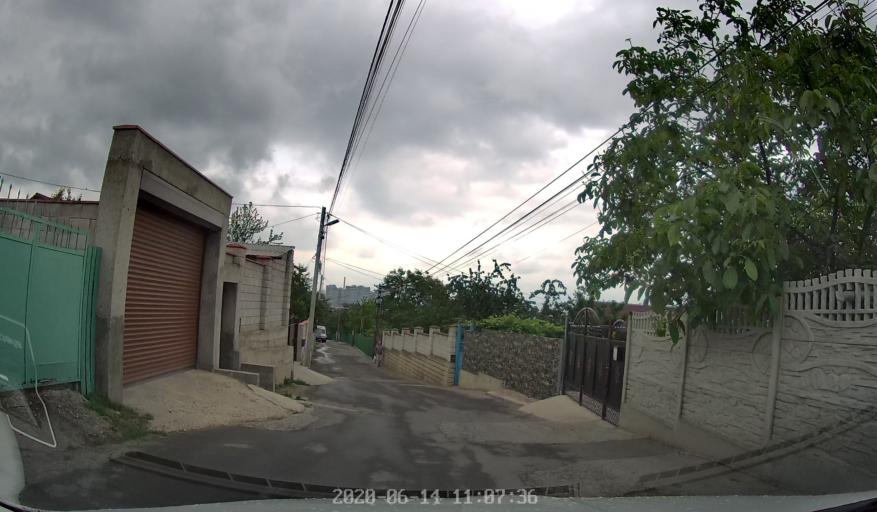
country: MD
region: Chisinau
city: Chisinau
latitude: 47.0448
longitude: 28.8368
